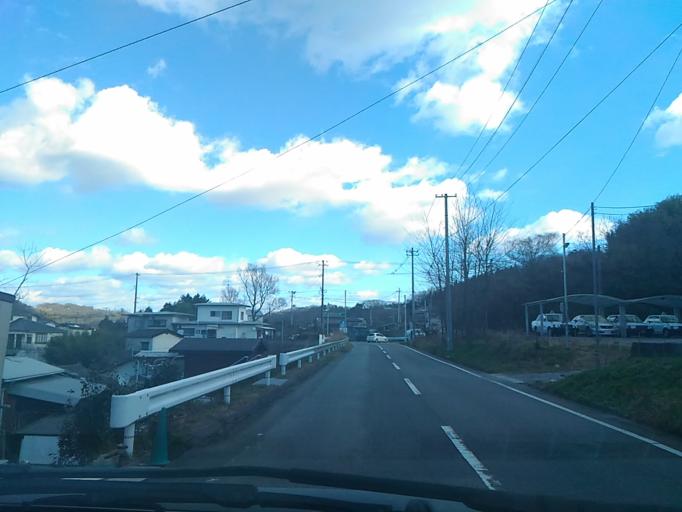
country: JP
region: Fukushima
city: Iwaki
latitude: 37.0110
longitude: 140.8334
